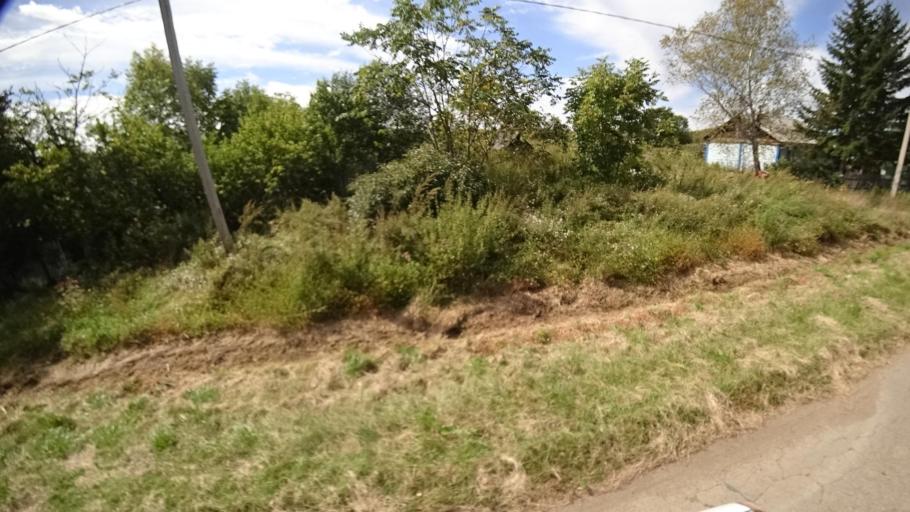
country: RU
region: Primorskiy
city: Yakovlevka
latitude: 44.7090
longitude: 133.6372
